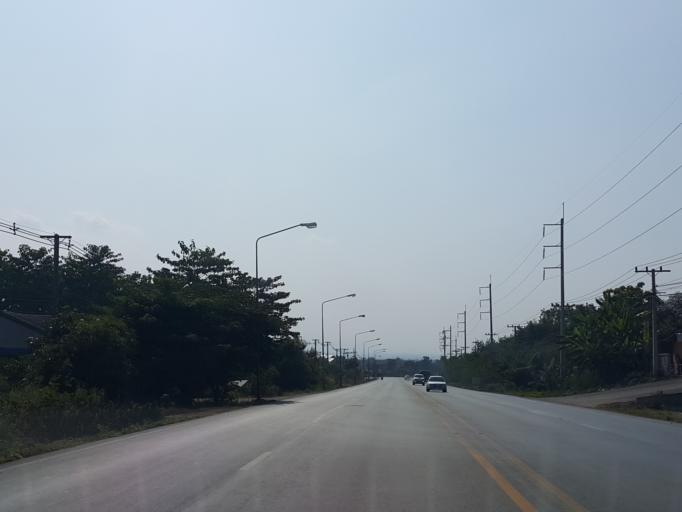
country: TH
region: Chiang Mai
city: Chom Thong
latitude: 18.3511
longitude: 98.6796
